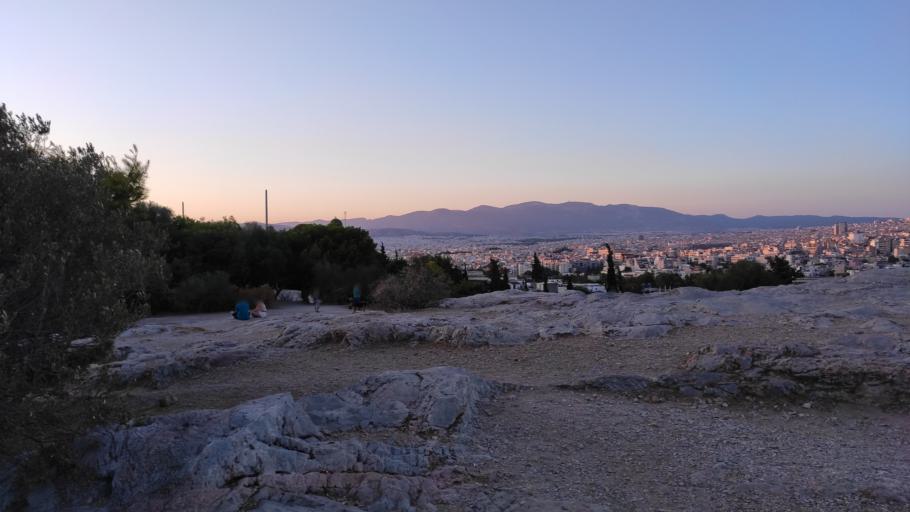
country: GR
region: Attica
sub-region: Nomarchia Athinas
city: Athens
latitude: 37.9710
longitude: 23.7192
